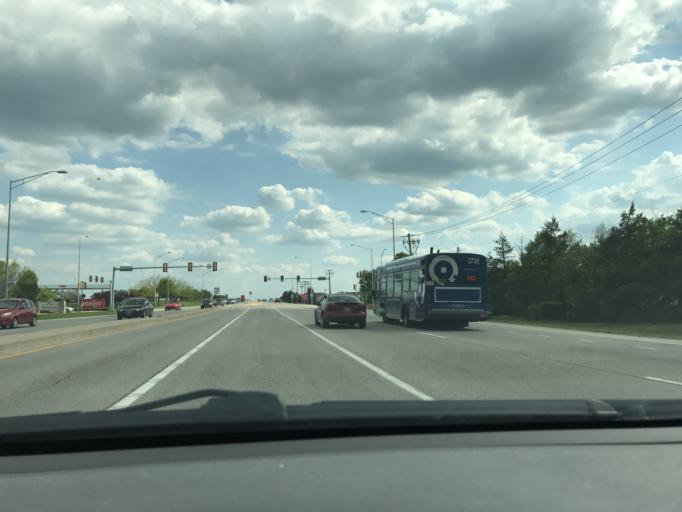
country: US
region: Illinois
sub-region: Kane County
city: South Elgin
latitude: 42.0158
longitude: -88.3364
